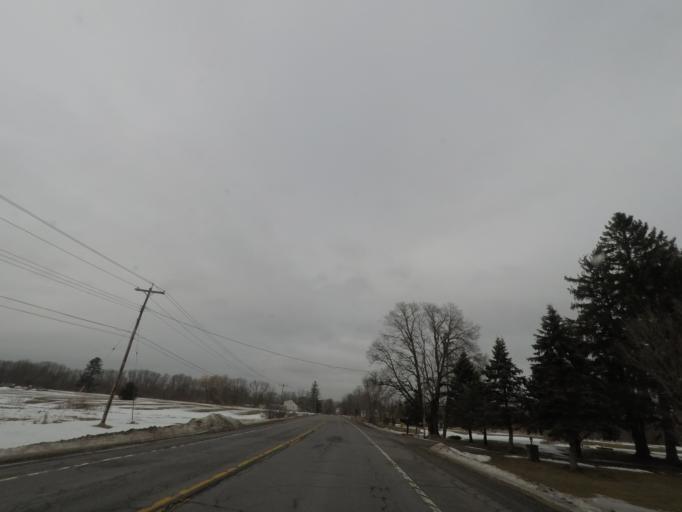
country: US
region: New York
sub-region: Schenectady County
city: Rotterdam
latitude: 42.7486
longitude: -73.9841
